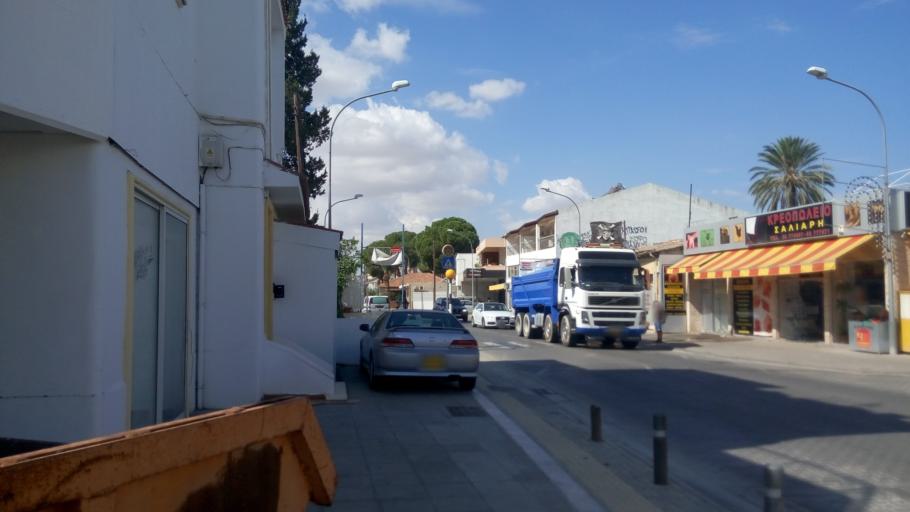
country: CY
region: Lefkosia
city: Nicosia
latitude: 35.1685
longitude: 33.3337
